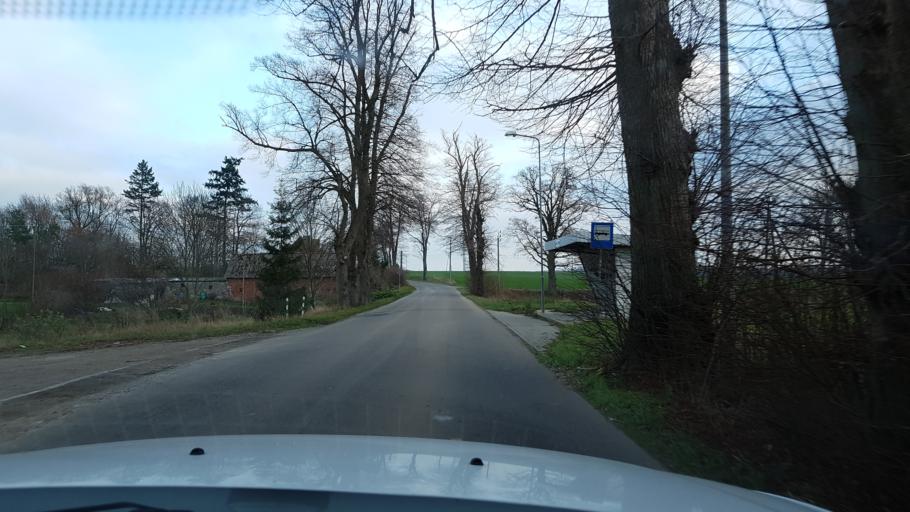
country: PL
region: West Pomeranian Voivodeship
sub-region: Powiat kolobrzeski
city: Goscino
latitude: 54.0549
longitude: 15.6852
